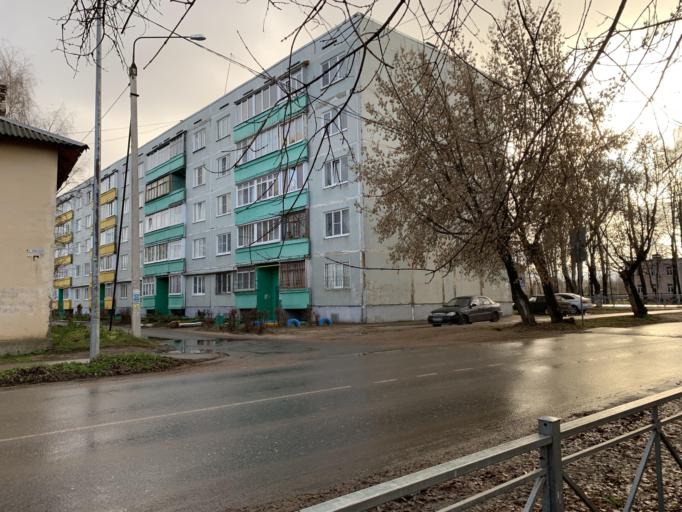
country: RU
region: Tverskaya
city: Likhoslavl'
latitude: 57.1254
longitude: 35.4615
